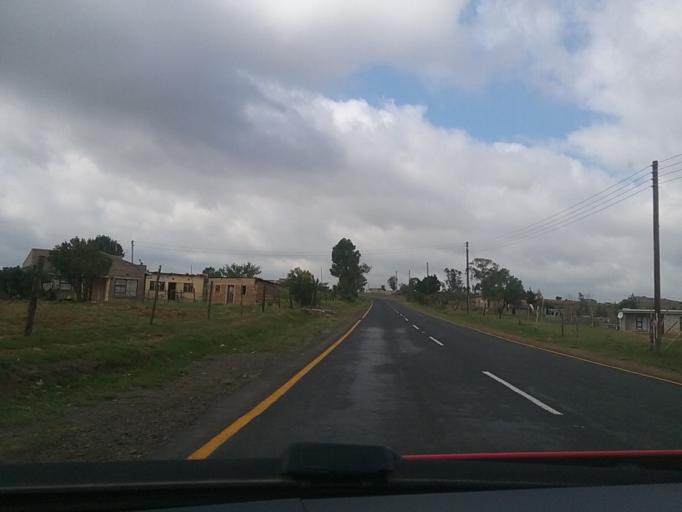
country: LS
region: Berea
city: Teyateyaneng
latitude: -29.1651
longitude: 27.7774
